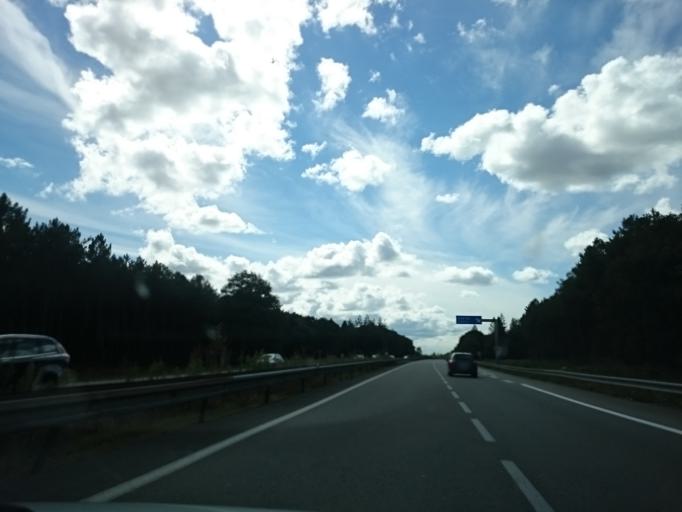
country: FR
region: Pays de la Loire
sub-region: Departement de la Loire-Atlantique
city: Le Cellier
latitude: 47.3409
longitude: -1.3771
